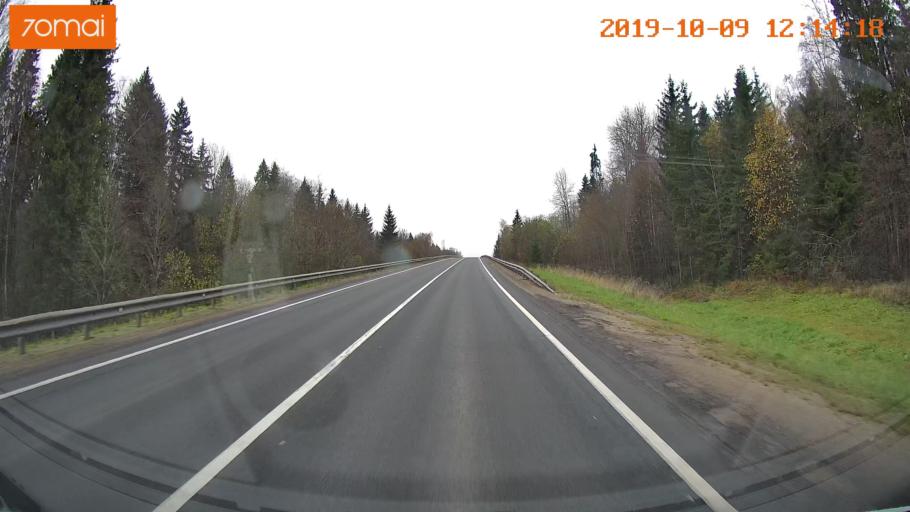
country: RU
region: Jaroslavl
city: Prechistoye
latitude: 58.4979
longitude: 40.3385
